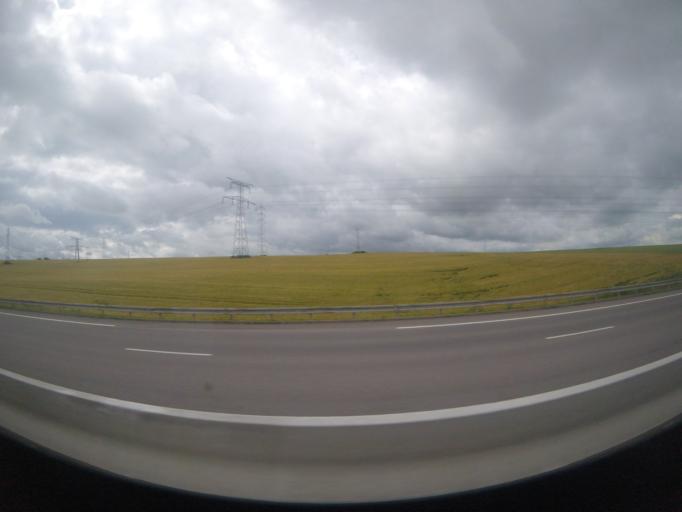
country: FR
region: Lorraine
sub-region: Departement de Meurthe-et-Moselle
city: Auboue
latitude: 49.2012
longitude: 5.9687
